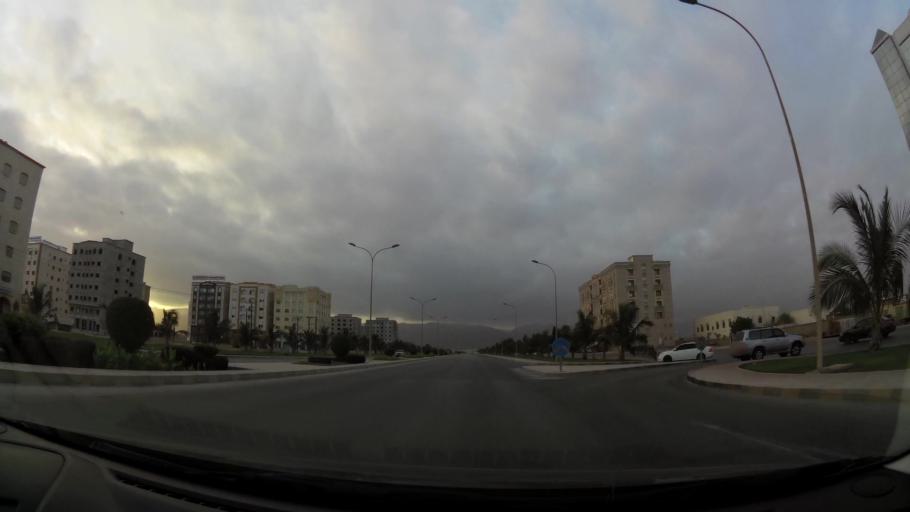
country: OM
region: Zufar
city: Salalah
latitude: 17.0231
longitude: 54.0333
